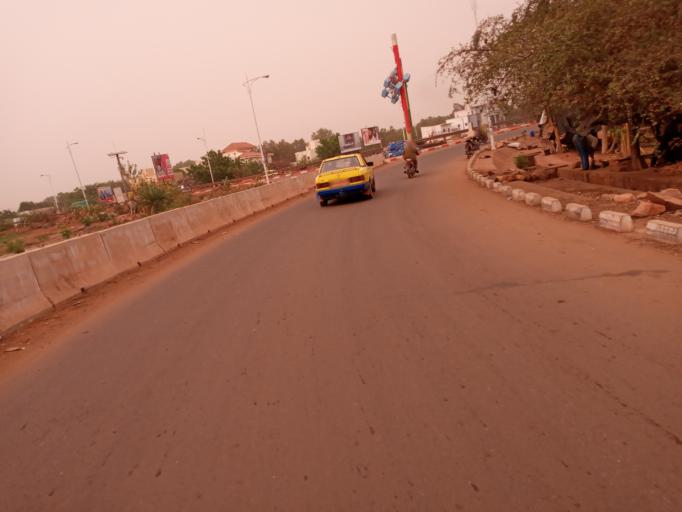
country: ML
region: Bamako
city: Bamako
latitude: 12.6503
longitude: -7.9307
